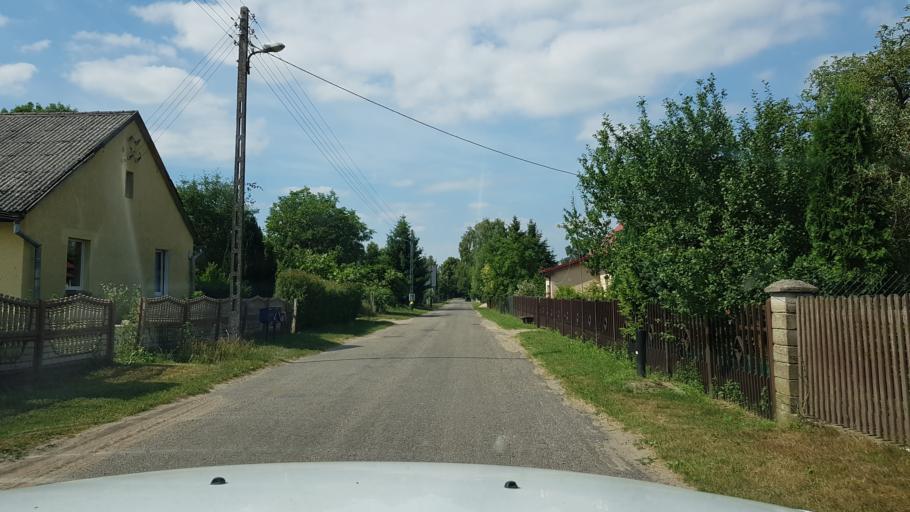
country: PL
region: West Pomeranian Voivodeship
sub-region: Powiat goleniowski
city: Mosty
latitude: 53.5757
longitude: 14.9786
